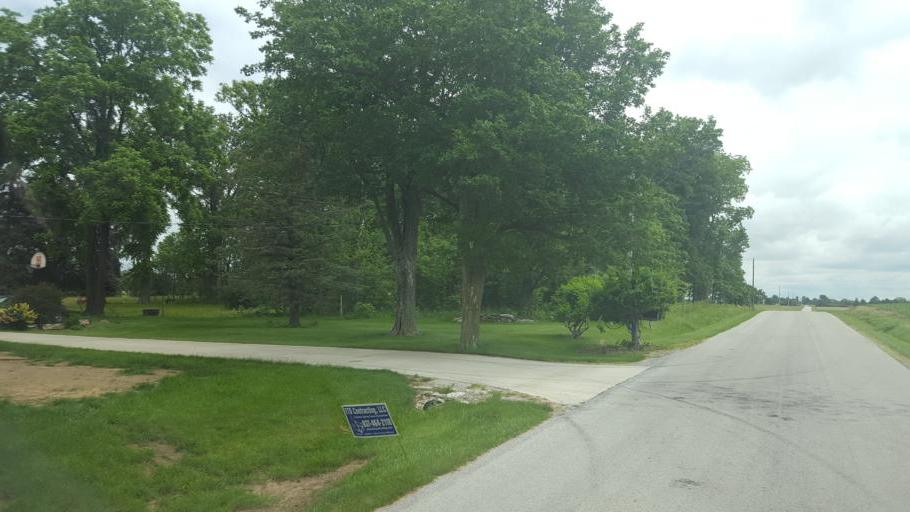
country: US
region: Ohio
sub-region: Crawford County
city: Bucyrus
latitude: 40.7752
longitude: -83.1039
